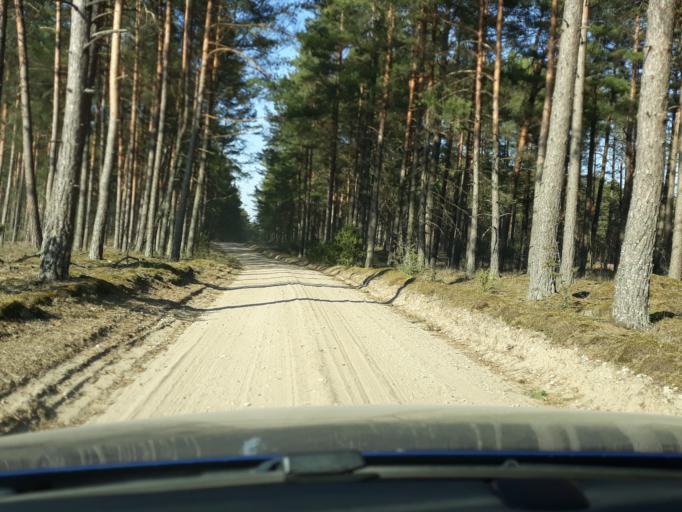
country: PL
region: Pomeranian Voivodeship
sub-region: Powiat bytowski
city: Lipnica
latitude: 53.9166
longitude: 17.4382
